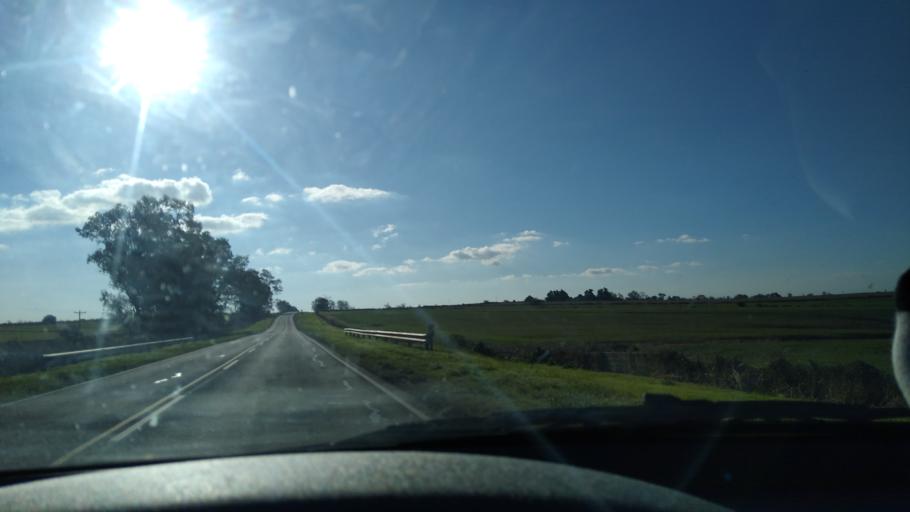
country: AR
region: Entre Rios
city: Diamante
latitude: -32.1272
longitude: -60.5614
